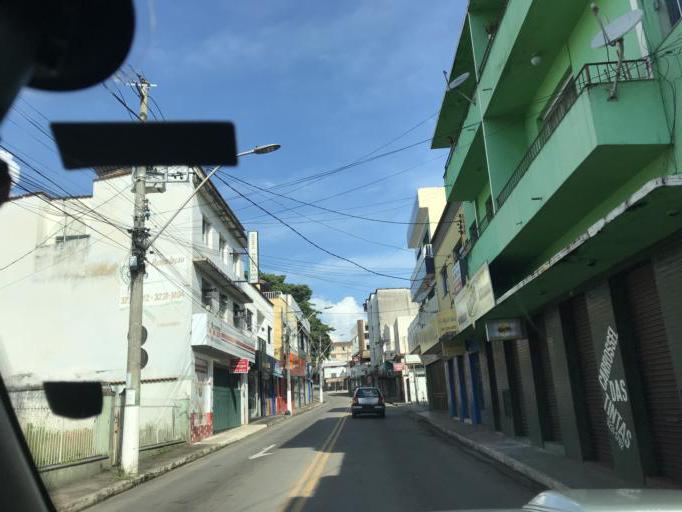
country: BR
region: Minas Gerais
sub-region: Tres Coracoes
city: Tres Coracoes
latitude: -21.6945
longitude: -45.2579
